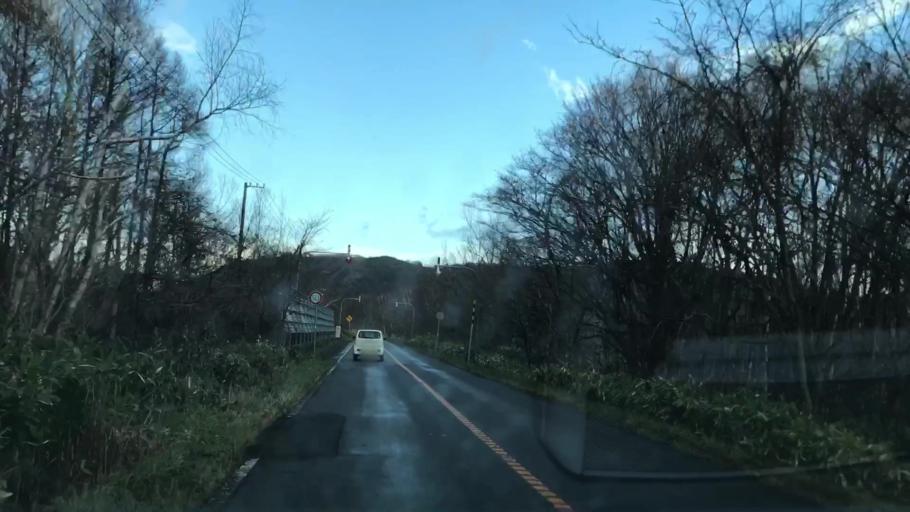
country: JP
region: Hokkaido
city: Yoichi
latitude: 43.3262
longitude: 140.5001
